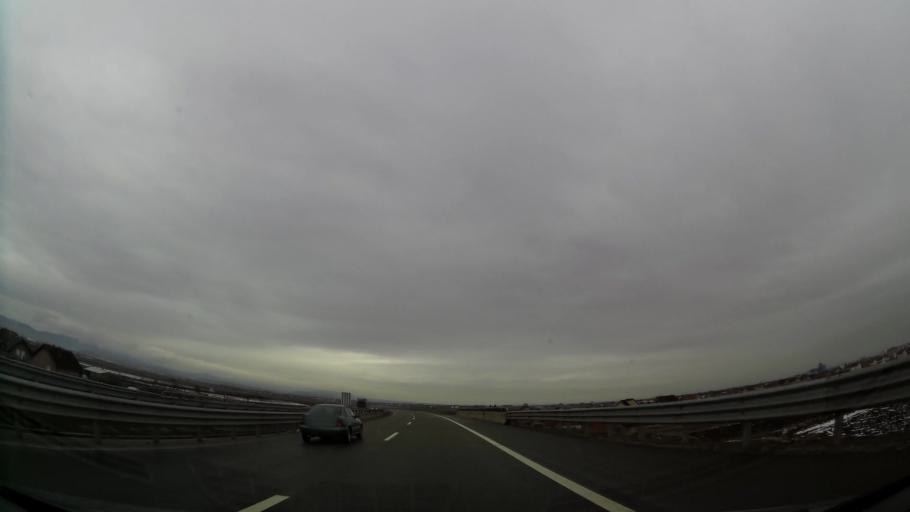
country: XK
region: Pristina
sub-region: Lipjan
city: Lipljan
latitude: 42.5355
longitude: 21.1356
